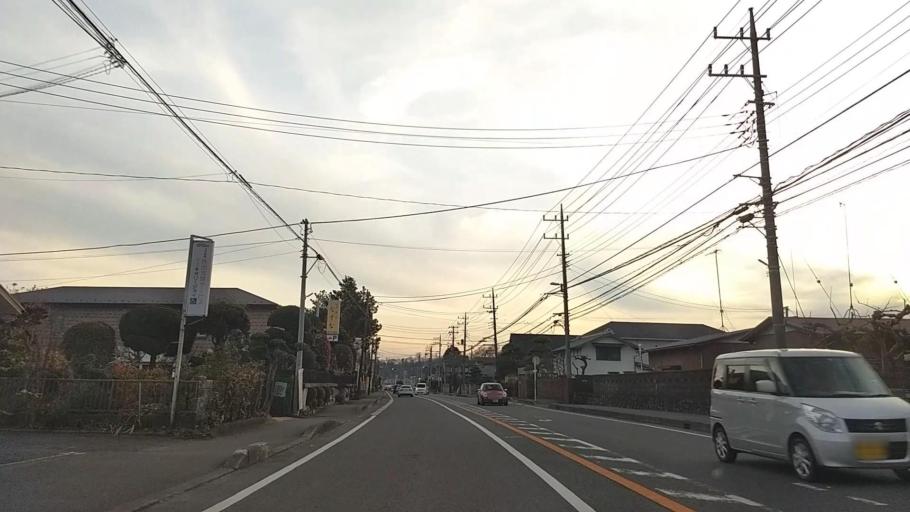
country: JP
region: Kanagawa
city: Atsugi
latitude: 35.4392
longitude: 139.3532
